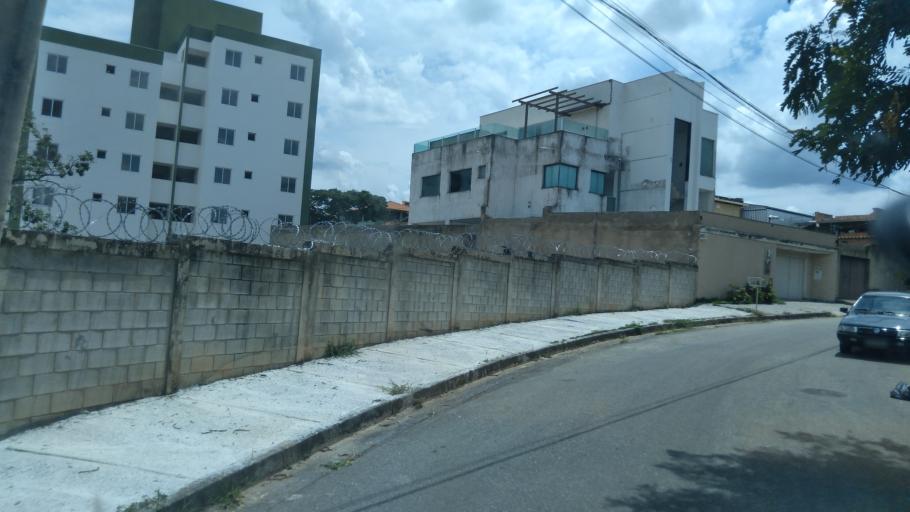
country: BR
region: Minas Gerais
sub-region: Belo Horizonte
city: Belo Horizonte
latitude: -19.8573
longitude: -43.8739
